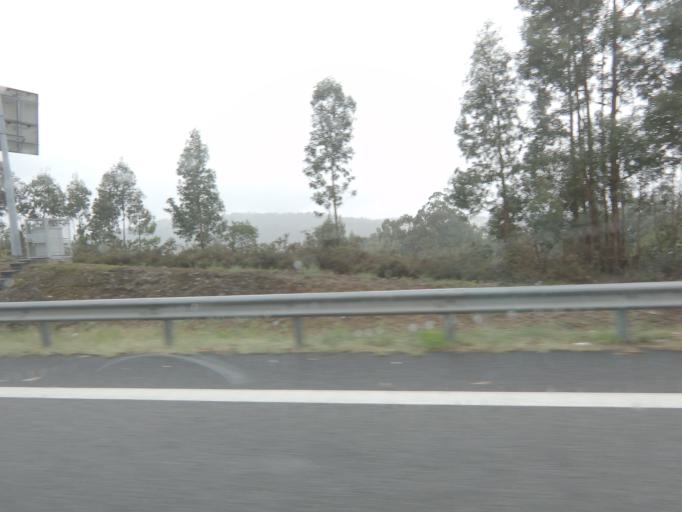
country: PT
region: Porto
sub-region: Valongo
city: Campo
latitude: 41.1925
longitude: -8.4828
